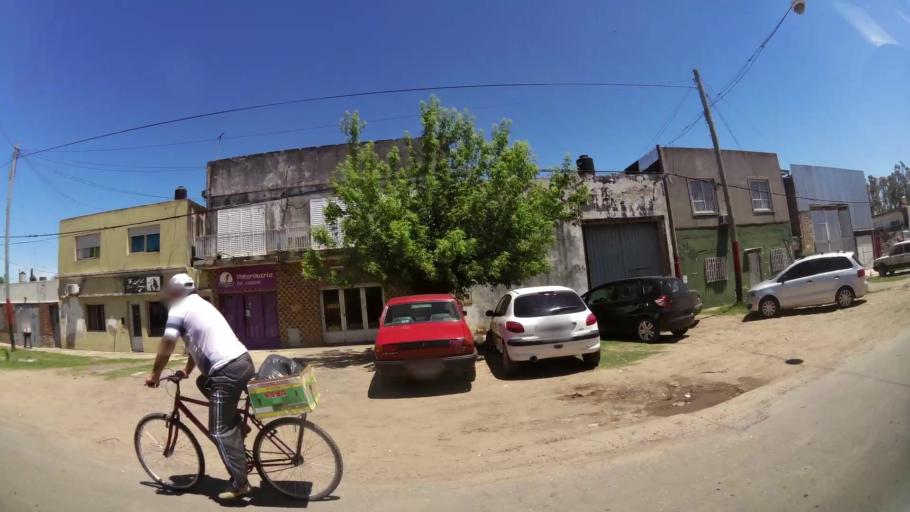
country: AR
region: Santa Fe
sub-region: Departamento de Rosario
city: Rosario
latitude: -32.9560
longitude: -60.7016
